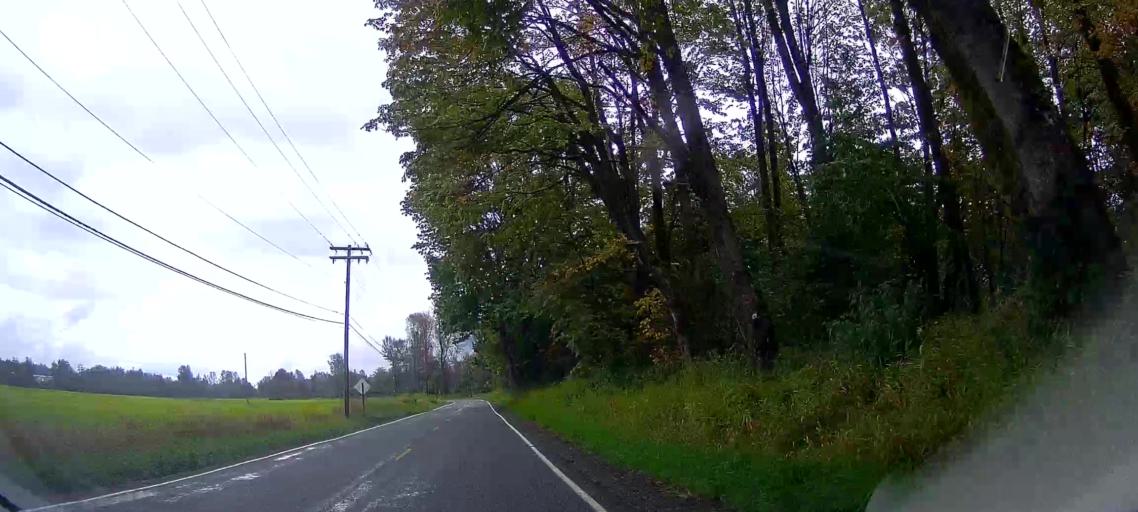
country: US
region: Washington
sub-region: Skagit County
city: Sedro-Woolley
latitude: 48.5272
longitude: -122.0186
